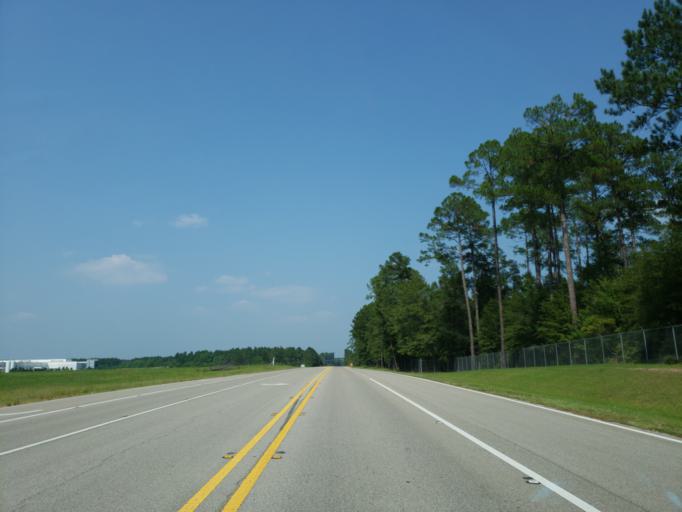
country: US
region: Mississippi
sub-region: Jones County
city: Ellisville
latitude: 31.5726
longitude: -89.2338
